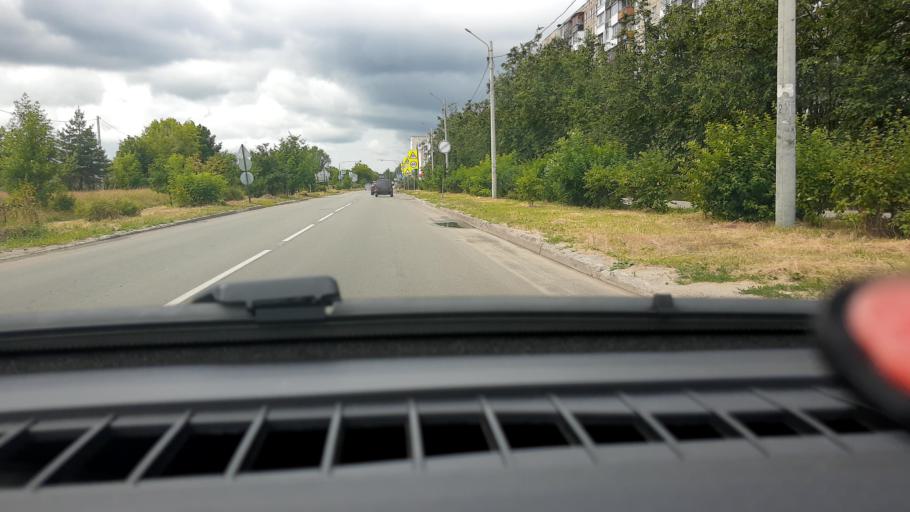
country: RU
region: Nizjnij Novgorod
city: Dzerzhinsk
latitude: 56.2217
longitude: 43.4063
